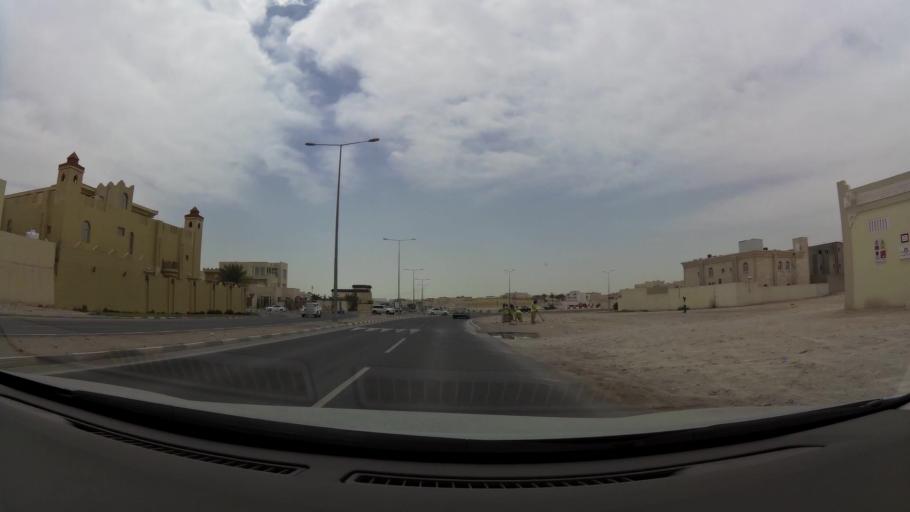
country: QA
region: Baladiyat ad Dawhah
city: Doha
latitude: 25.2223
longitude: 51.4688
